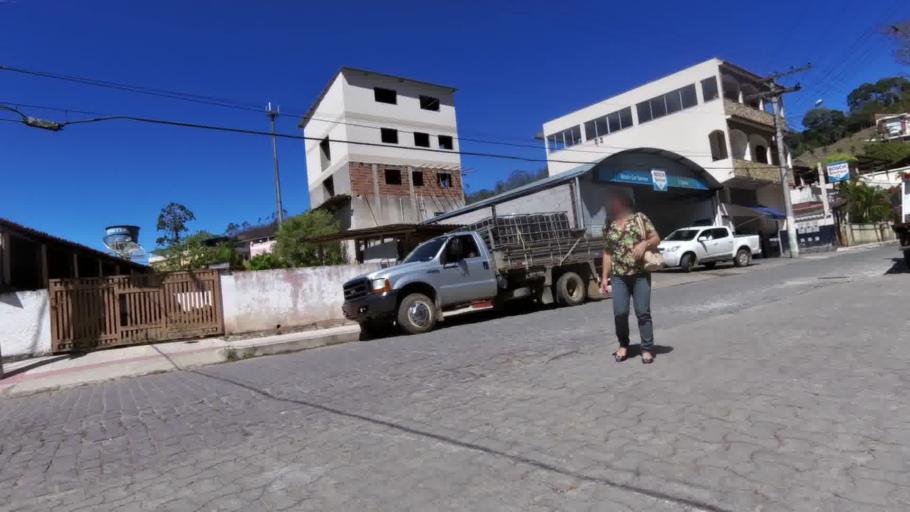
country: BR
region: Espirito Santo
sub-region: Vargem Alta
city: Vargem Alta
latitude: -20.6738
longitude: -41.0128
